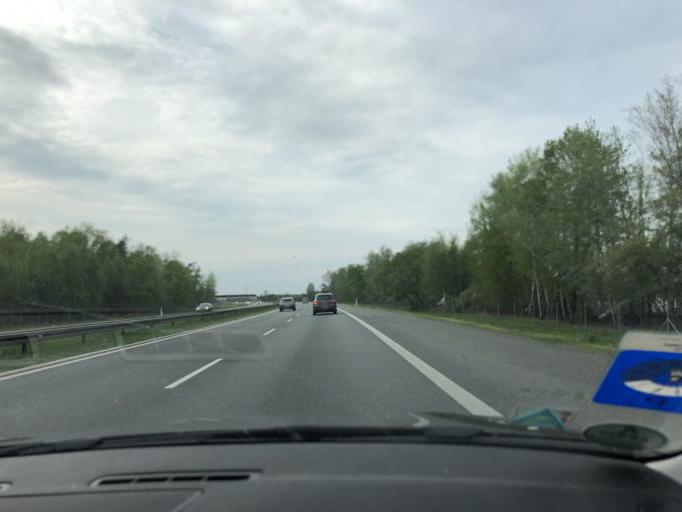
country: PL
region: Opole Voivodeship
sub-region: Powiat brzeski
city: Lewin Brzeski
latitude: 50.7027
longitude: 17.6169
